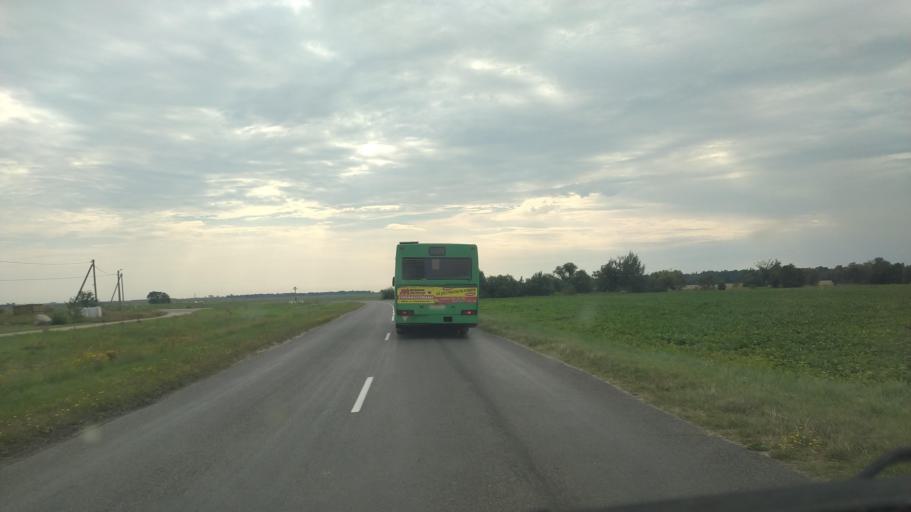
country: BY
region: Brest
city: Byaroza
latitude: 52.5773
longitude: 24.8599
